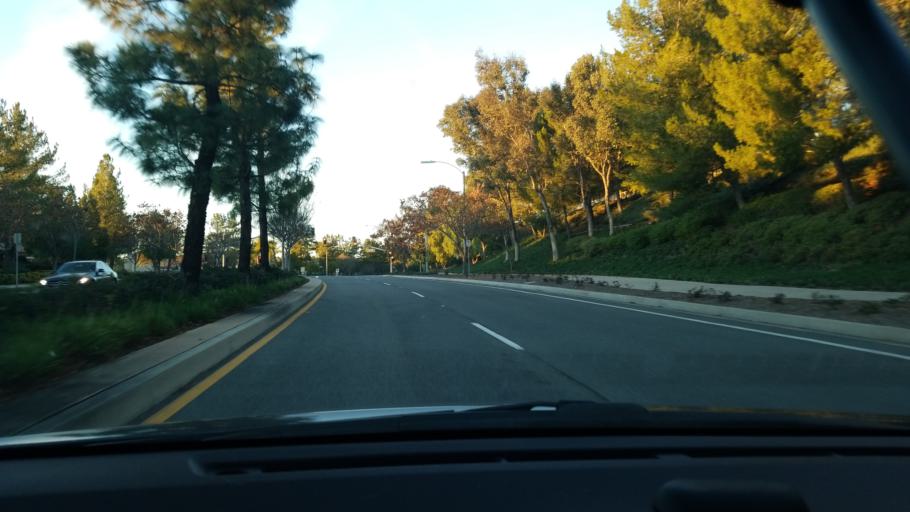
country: US
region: California
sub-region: Riverside County
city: Temecula
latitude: 33.4904
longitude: -117.0955
